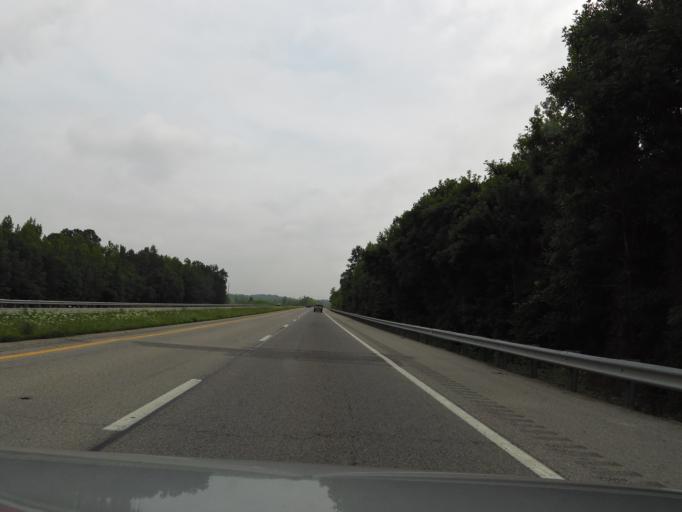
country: US
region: Kentucky
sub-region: Ohio County
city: Beaver Dam
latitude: 37.3443
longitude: -86.9353
